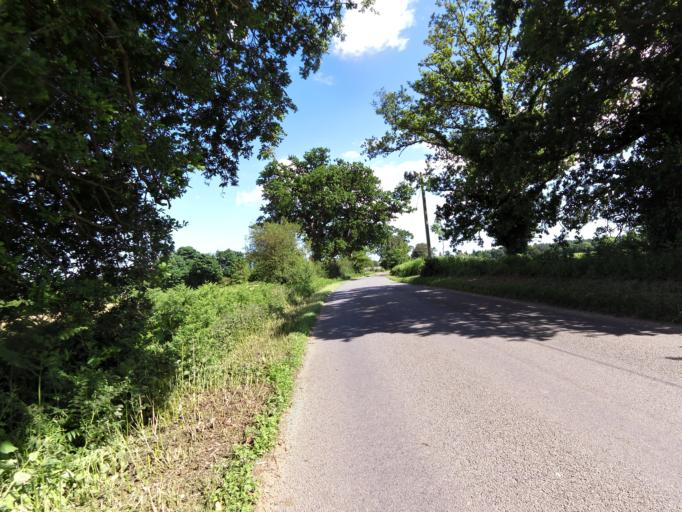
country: GB
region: England
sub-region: Suffolk
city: Kesgrave
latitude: 52.0170
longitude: 1.2217
